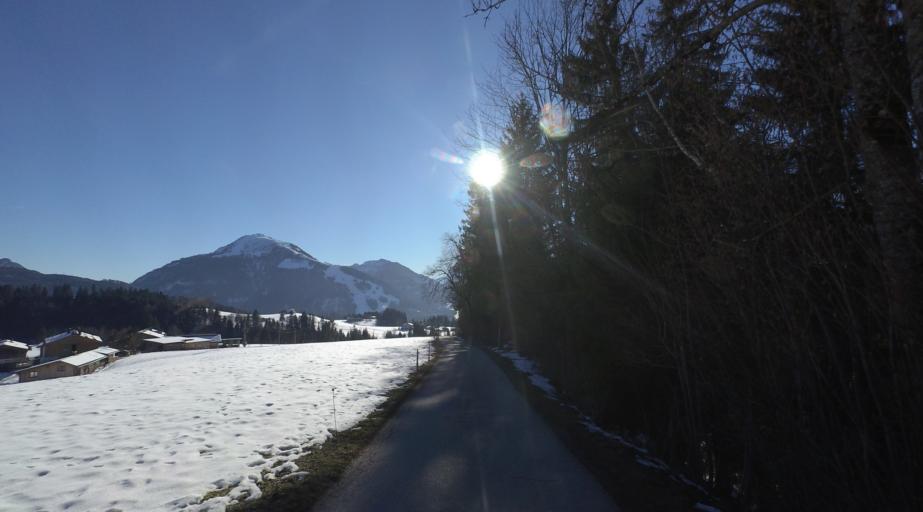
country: AT
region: Tyrol
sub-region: Politischer Bezirk Kitzbuhel
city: Kossen
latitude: 47.6809
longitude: 12.4285
